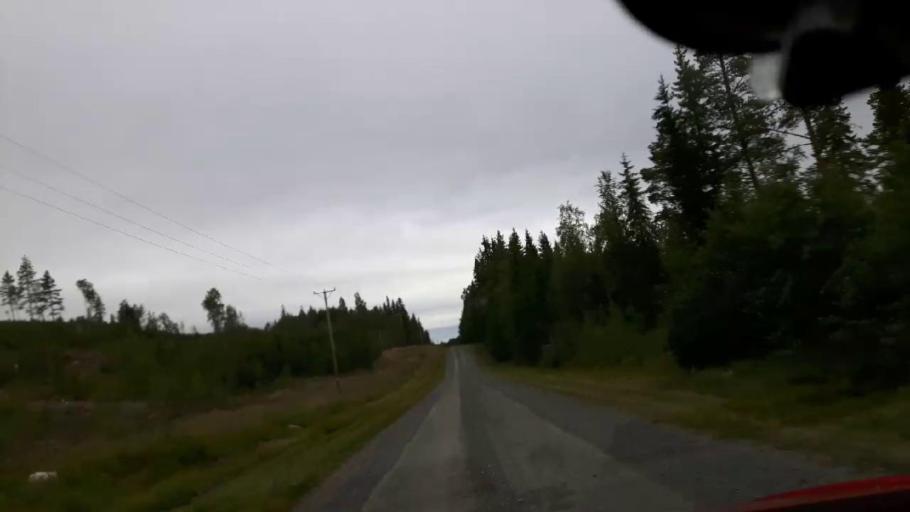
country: SE
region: Vaesternorrland
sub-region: Ange Kommun
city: Ange
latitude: 62.8503
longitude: 15.9308
